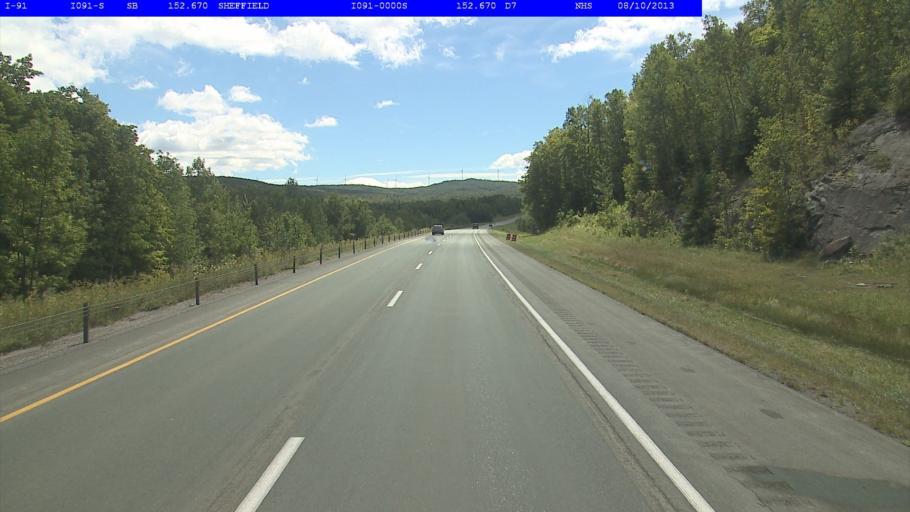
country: US
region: Vermont
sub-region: Caledonia County
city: Lyndonville
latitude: 44.7010
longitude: -72.1466
